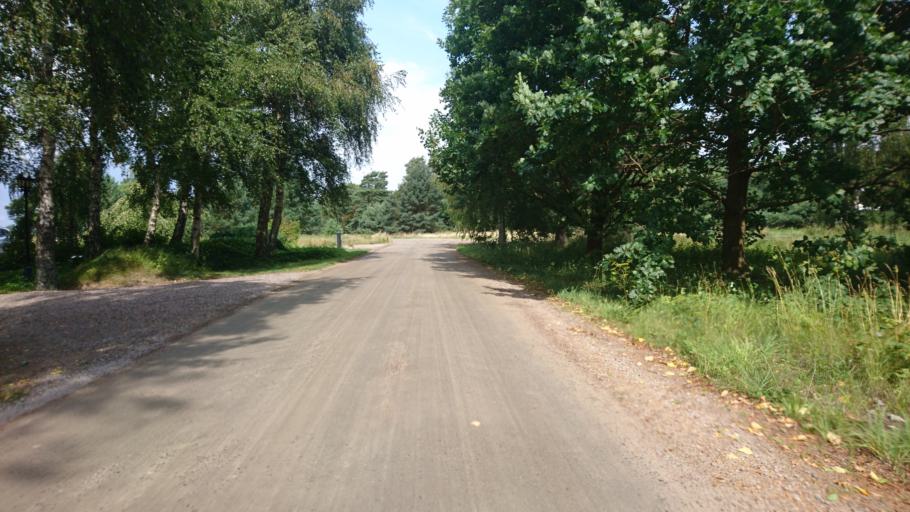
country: SE
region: Skane
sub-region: Vellinge Kommun
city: Ljunghusen
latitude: 55.3996
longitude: 12.9103
